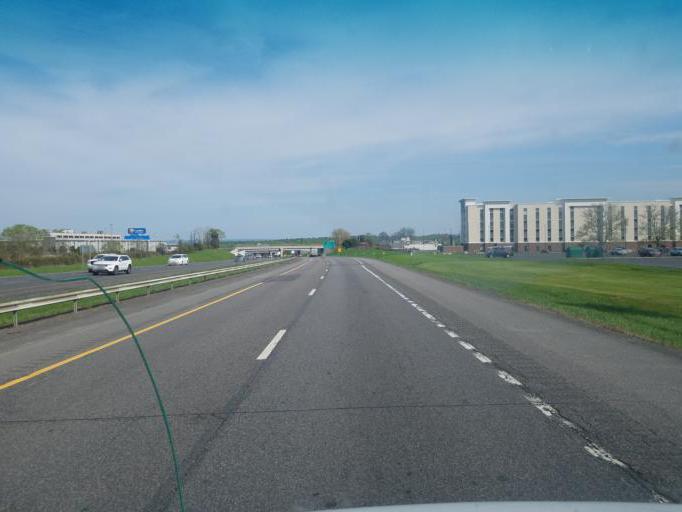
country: US
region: New York
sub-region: Onondaga County
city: Galeville
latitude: 43.0969
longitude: -76.1733
